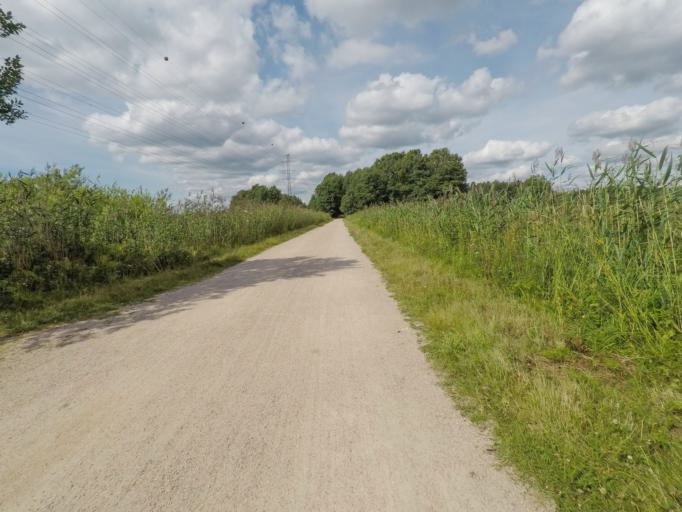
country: FI
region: Uusimaa
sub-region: Helsinki
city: Vantaa
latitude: 60.2145
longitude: 25.0184
